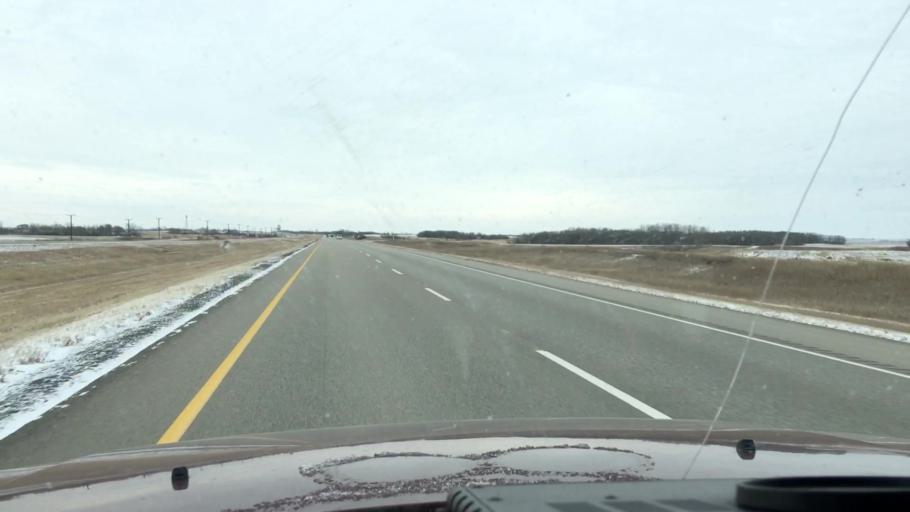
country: CA
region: Saskatchewan
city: Watrous
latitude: 51.3915
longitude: -106.1679
